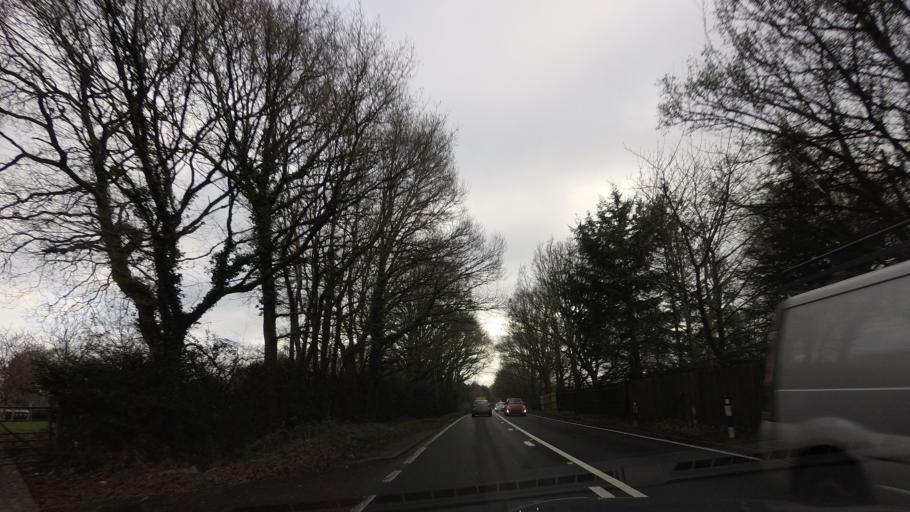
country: GB
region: England
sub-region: East Sussex
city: Wadhurst
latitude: 51.0813
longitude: 0.4170
